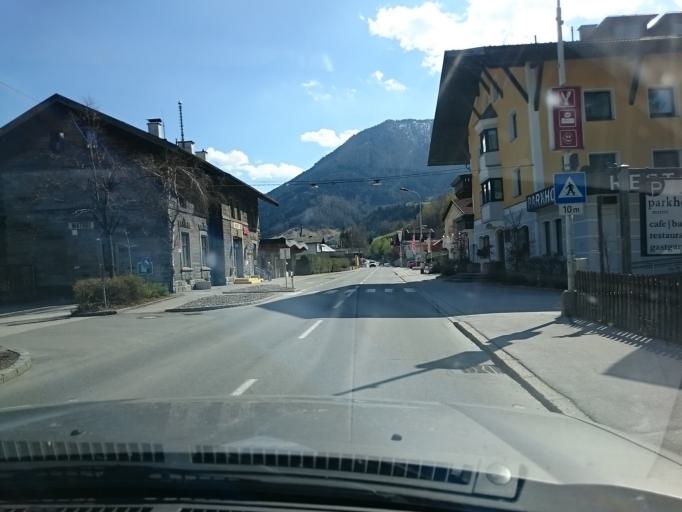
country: AT
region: Tyrol
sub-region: Politischer Bezirk Innsbruck Land
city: Matrei am Brenner
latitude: 47.1277
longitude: 11.4525
